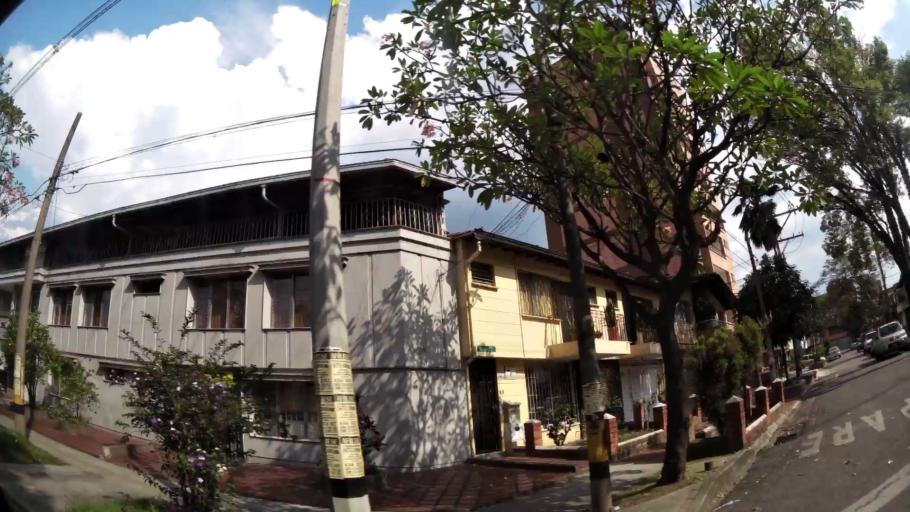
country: CO
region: Antioquia
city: Medellin
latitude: 6.2365
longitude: -75.5926
